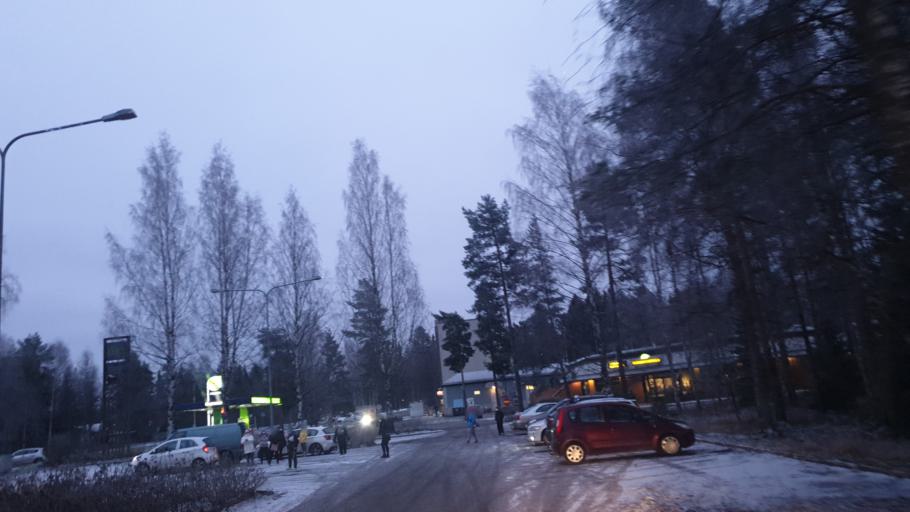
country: FI
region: Southern Ostrobothnia
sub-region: Seinaejoki
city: Seinaejoki
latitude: 62.7712
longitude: 22.8763
